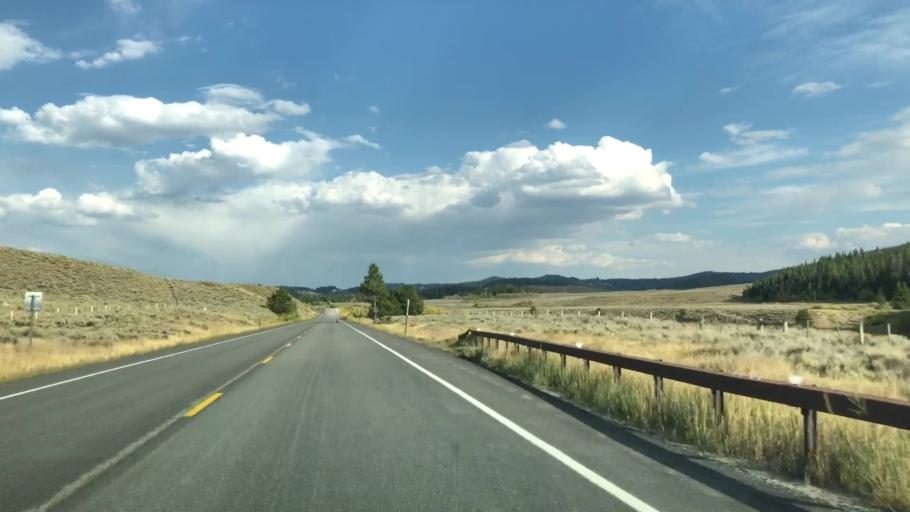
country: US
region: Wyoming
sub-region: Sublette County
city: Pinedale
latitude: 43.1503
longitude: -110.2745
